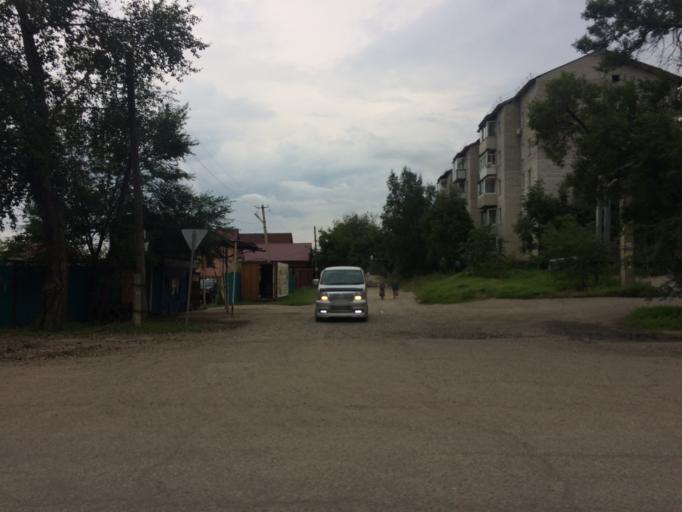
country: RU
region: Primorskiy
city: Dal'nerechensk
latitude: 45.9350
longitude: 133.7384
